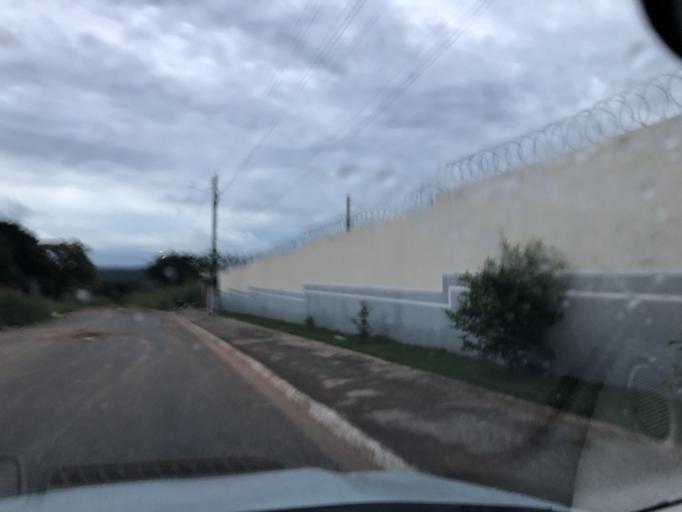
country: BR
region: Goias
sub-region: Luziania
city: Luziania
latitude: -16.1154
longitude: -47.9864
